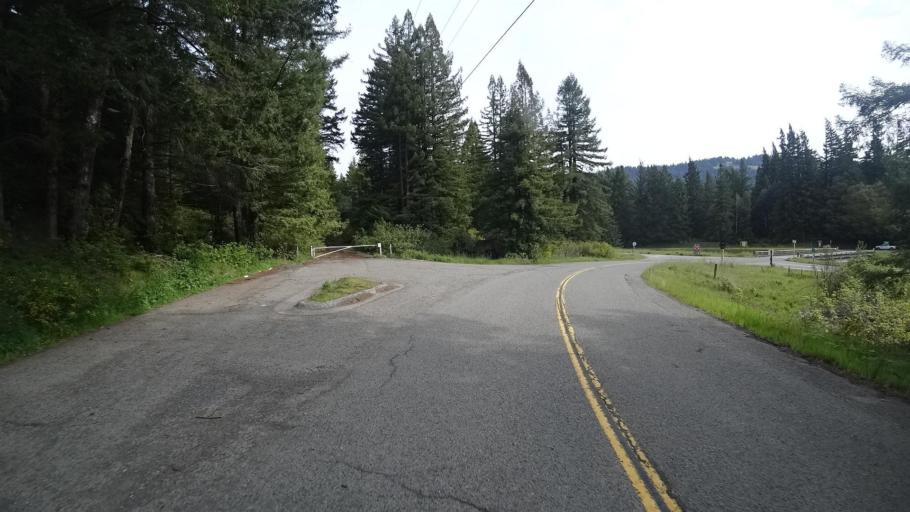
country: US
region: California
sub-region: Humboldt County
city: Redway
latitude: 40.2504
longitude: -123.8329
